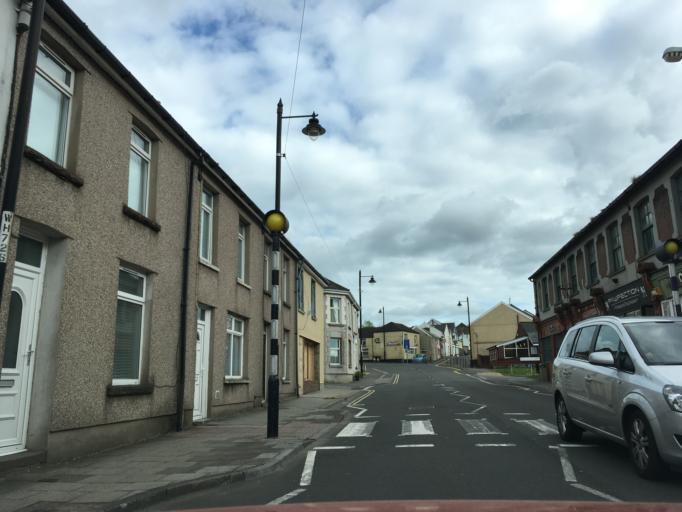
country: GB
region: Wales
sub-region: Caerphilly County Borough
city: Nelson
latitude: 51.6509
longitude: -3.2821
